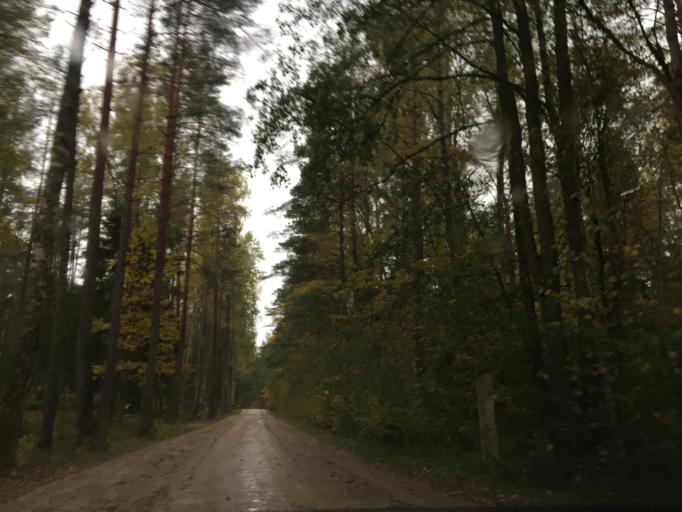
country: LV
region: Engure
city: Smarde
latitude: 56.9289
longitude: 23.4759
